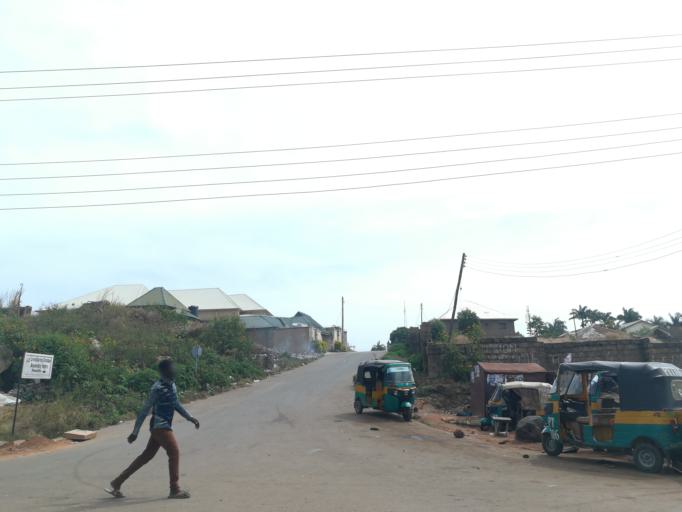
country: NG
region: Plateau
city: Jos
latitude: 9.8890
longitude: 8.8647
